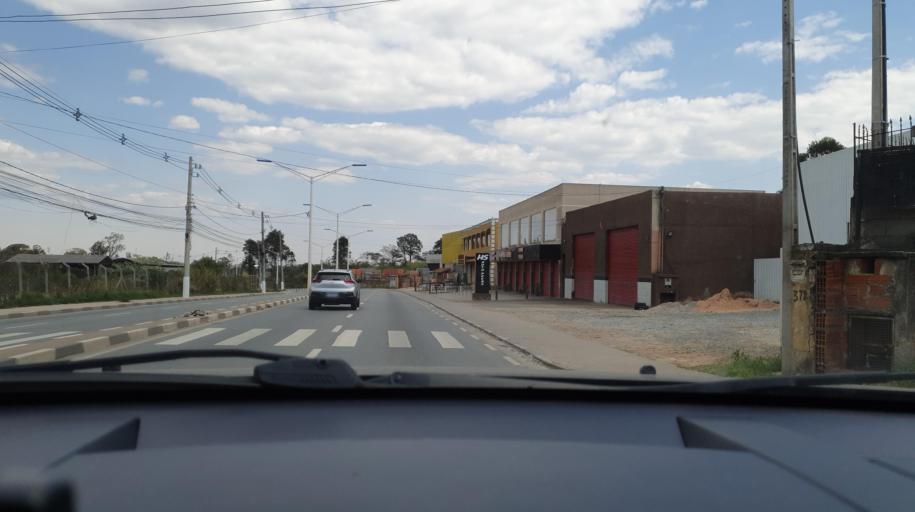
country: BR
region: Sao Paulo
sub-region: Vargem Grande Paulista
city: Vargem Grande Paulista
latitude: -23.6576
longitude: -46.9997
